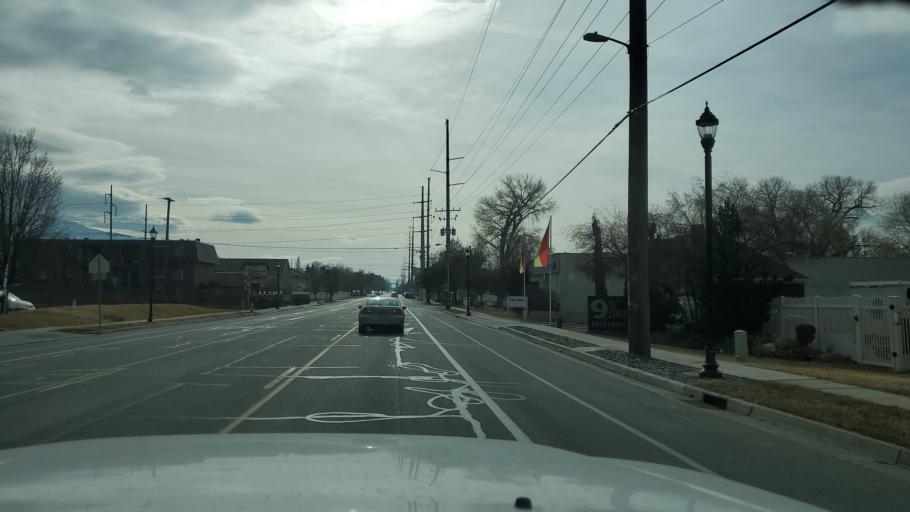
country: US
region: Utah
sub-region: Salt Lake County
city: Millcreek
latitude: 40.6907
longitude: -111.8655
